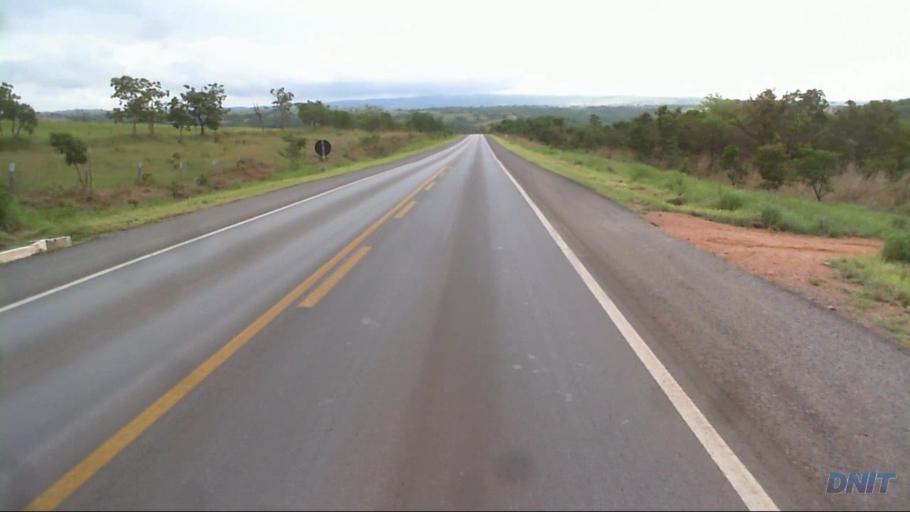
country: BR
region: Goias
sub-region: Padre Bernardo
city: Padre Bernardo
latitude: -15.2156
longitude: -48.5983
